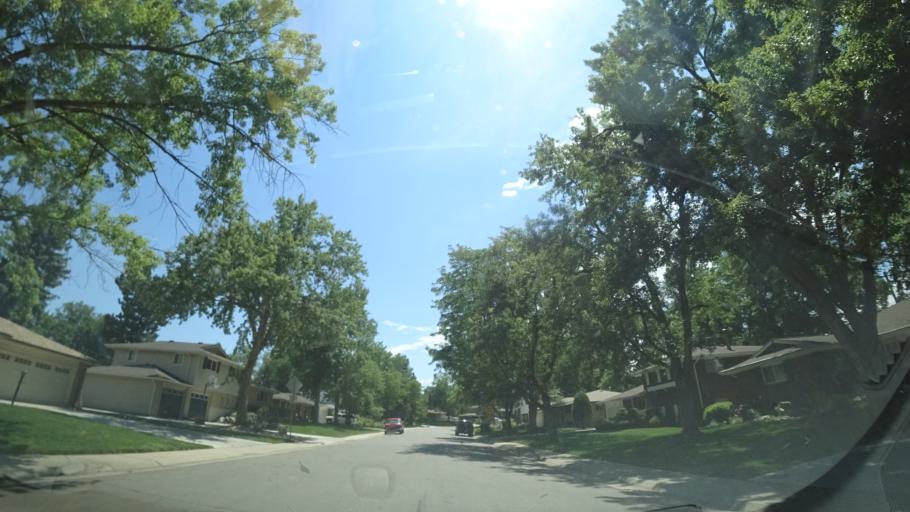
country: US
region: Colorado
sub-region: Jefferson County
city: Lakewood
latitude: 39.6957
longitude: -105.0931
